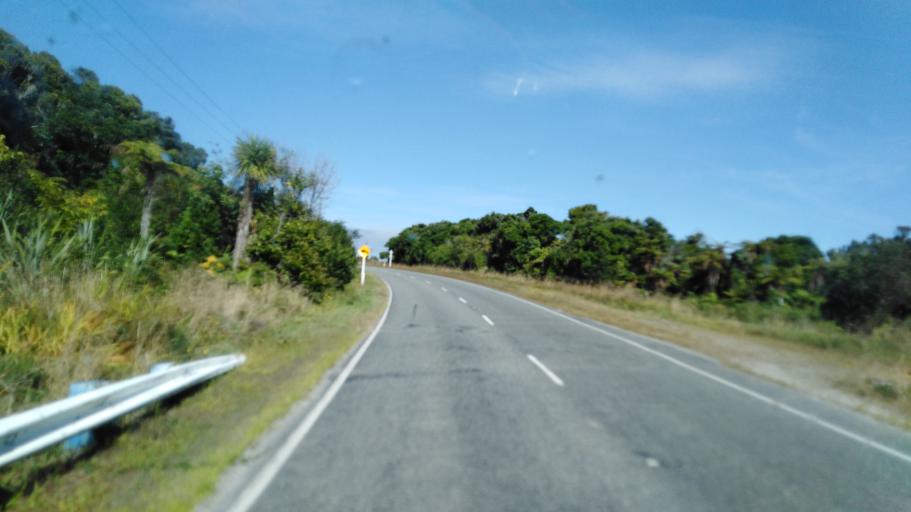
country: NZ
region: West Coast
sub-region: Buller District
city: Westport
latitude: -41.2904
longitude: 172.0974
